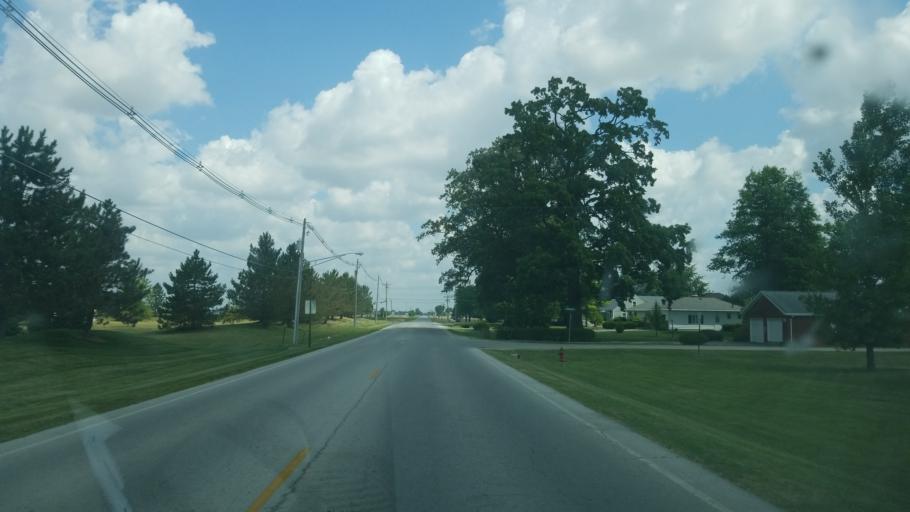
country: US
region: Ohio
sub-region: Auglaize County
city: Wapakoneta
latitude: 40.5896
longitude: -84.2029
